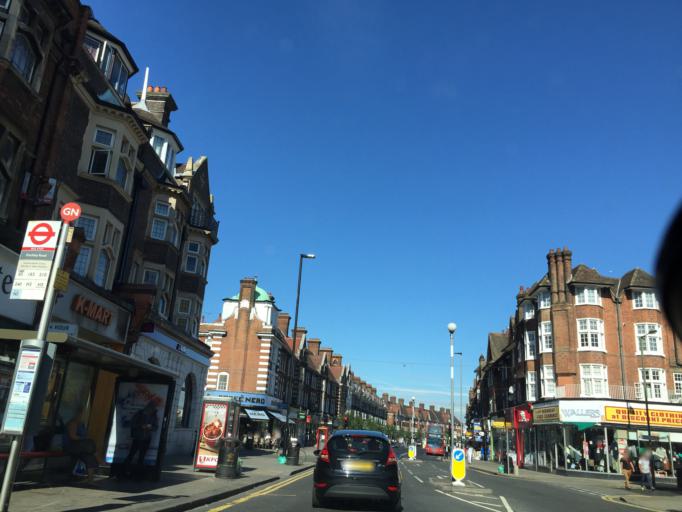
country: GB
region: England
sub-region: Greater London
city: Belsize Park
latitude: 51.5719
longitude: -0.1961
